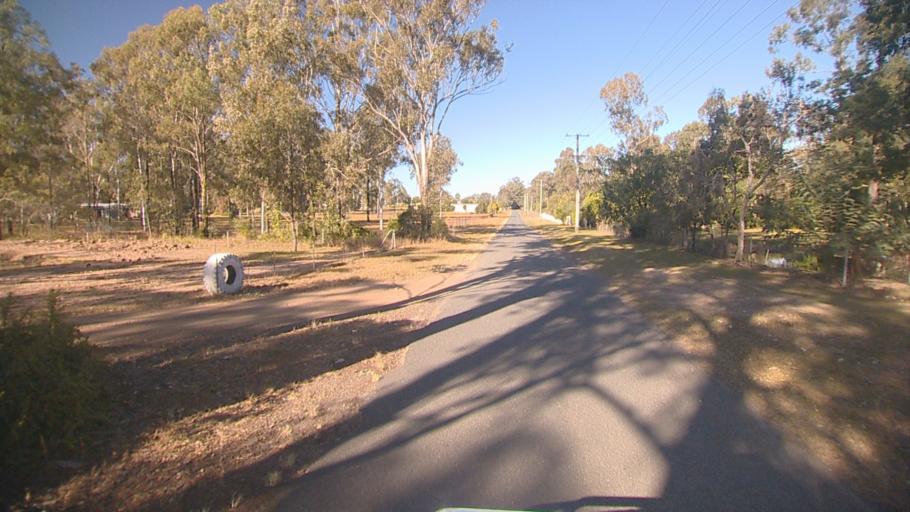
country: AU
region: Queensland
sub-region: Logan
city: North Maclean
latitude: -27.7550
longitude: 153.0338
